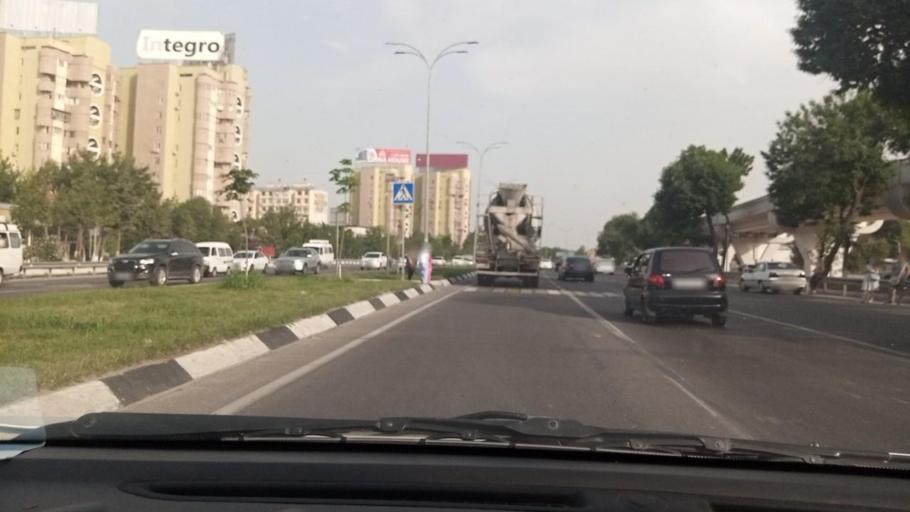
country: UZ
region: Toshkent Shahri
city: Bektemir
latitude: 41.2910
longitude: 69.3577
